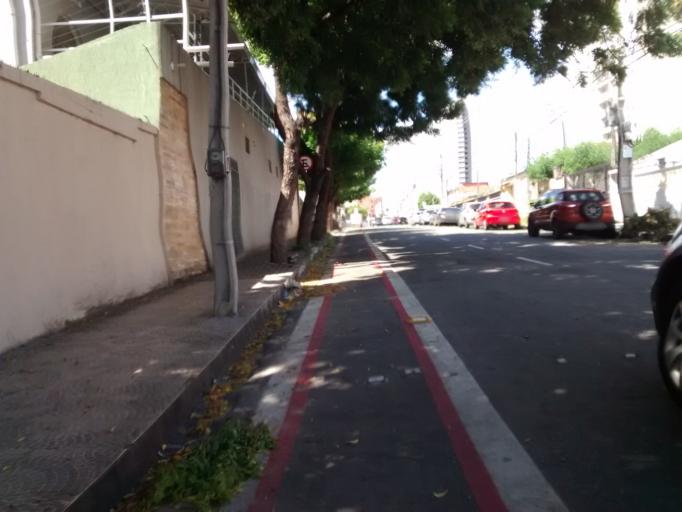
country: BR
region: Ceara
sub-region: Fortaleza
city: Fortaleza
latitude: -3.7326
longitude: -38.5593
